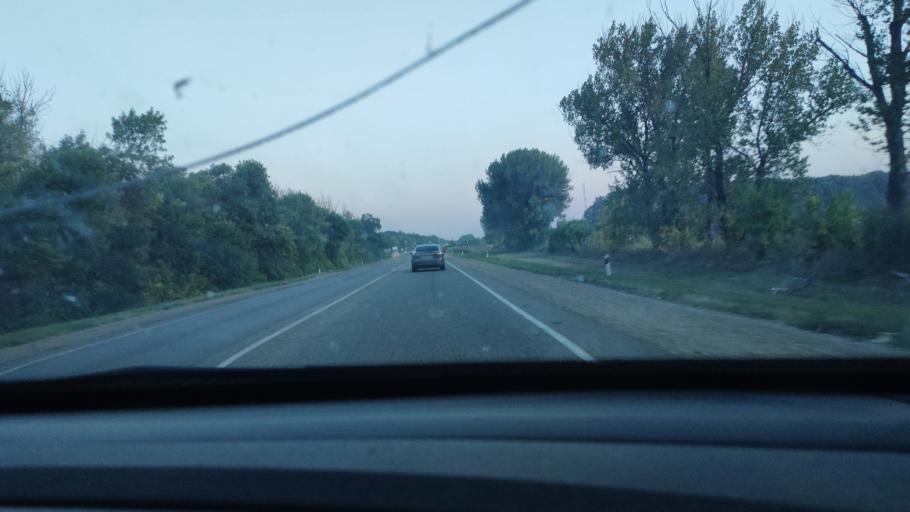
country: RU
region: Krasnodarskiy
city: Medvedovskaya
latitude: 45.4579
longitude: 38.9872
